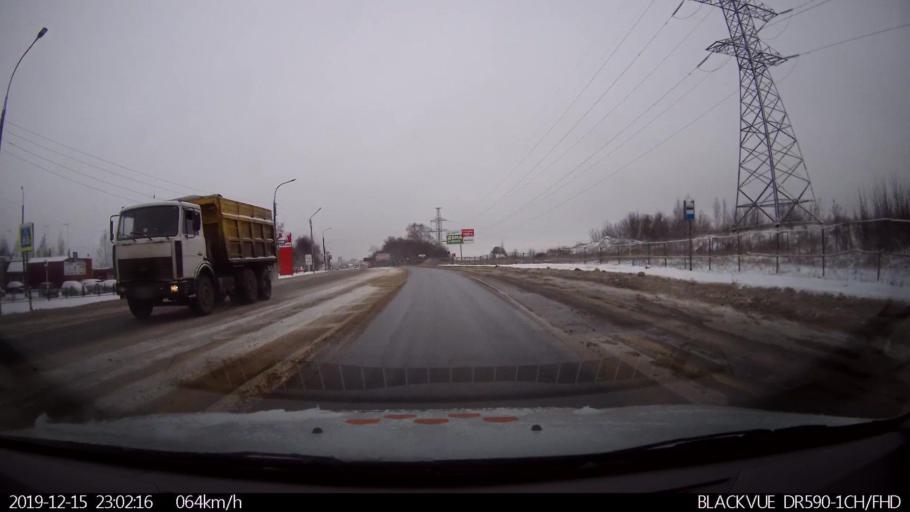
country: RU
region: Nizjnij Novgorod
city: Afonino
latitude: 56.2473
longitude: 44.1007
